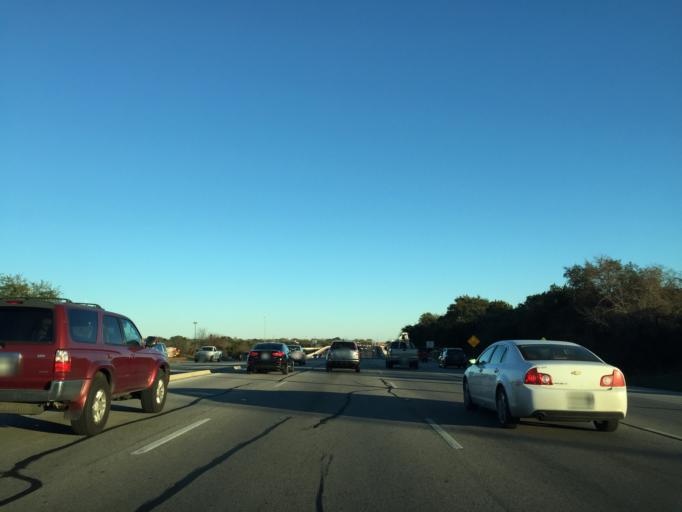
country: US
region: Texas
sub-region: Travis County
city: Wells Branch
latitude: 30.4238
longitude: -97.7111
